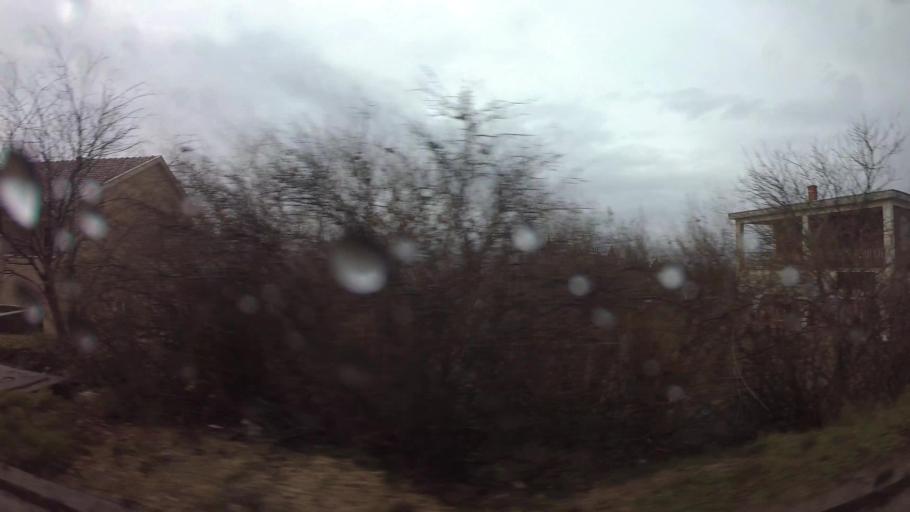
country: BA
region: Federation of Bosnia and Herzegovina
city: Rodoc
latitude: 43.3086
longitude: 17.8425
